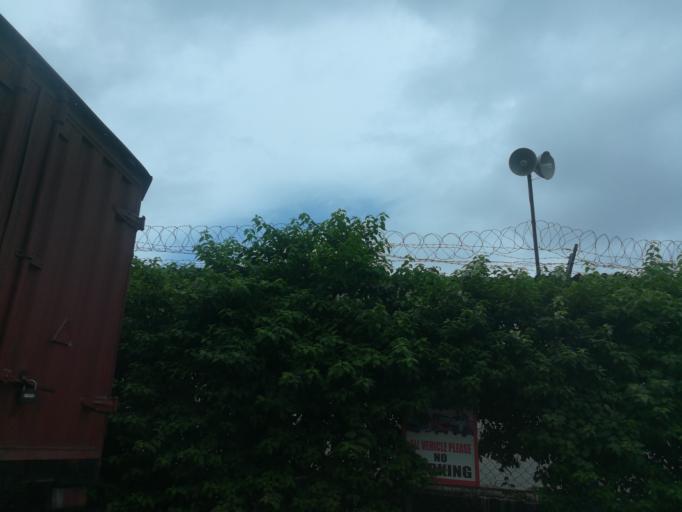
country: NG
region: Lagos
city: Ikeja
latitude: 6.6117
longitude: 3.3418
